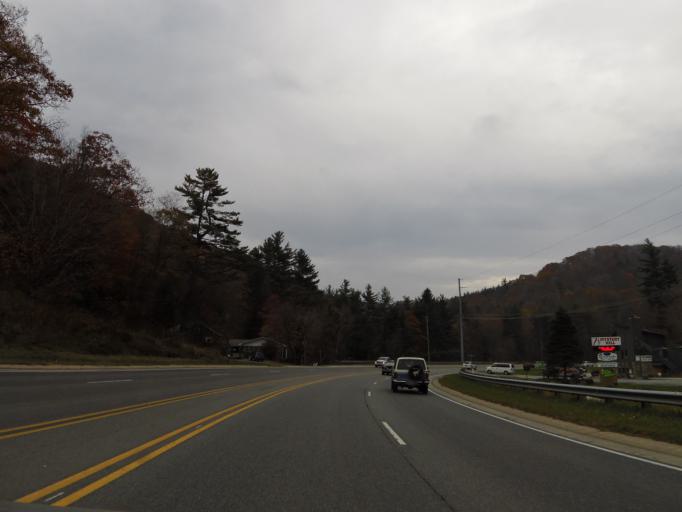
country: US
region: North Carolina
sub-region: Watauga County
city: Blowing Rock
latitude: 36.1640
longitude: -81.6440
